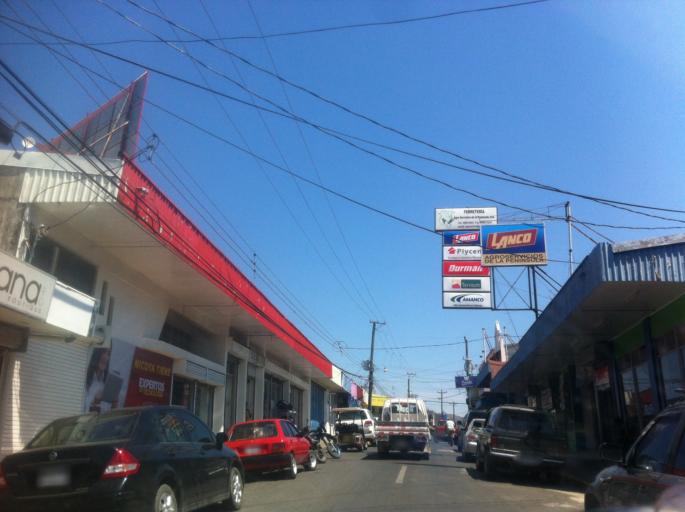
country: CR
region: Guanacaste
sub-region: Canton de Nicoya
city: Nicoya
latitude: 10.1381
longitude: -85.4485
